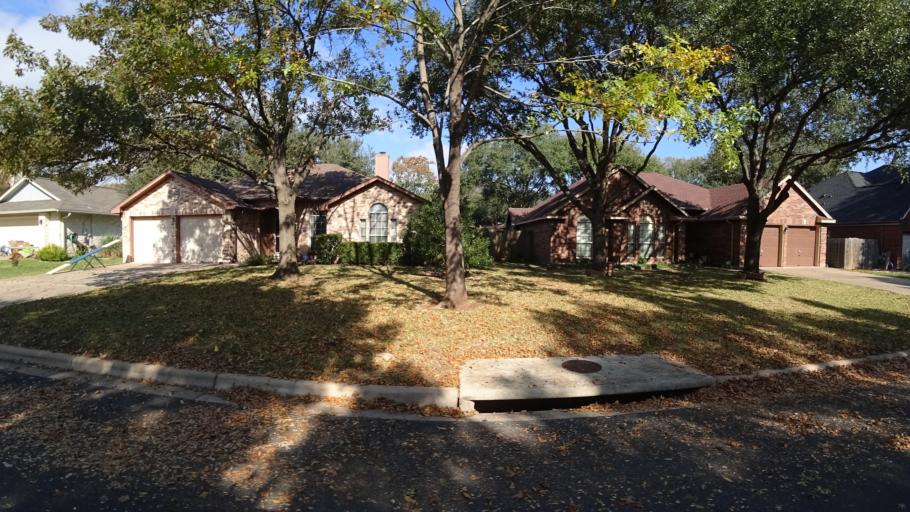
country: US
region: Texas
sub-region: Travis County
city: Shady Hollow
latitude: 30.1711
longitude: -97.8694
